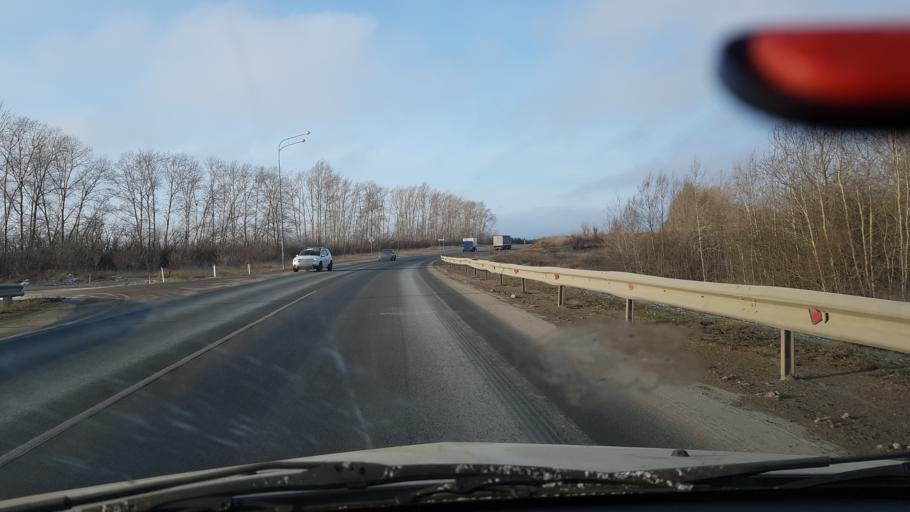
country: RU
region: Tatarstan
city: Laishevo
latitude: 55.3914
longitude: 49.7936
